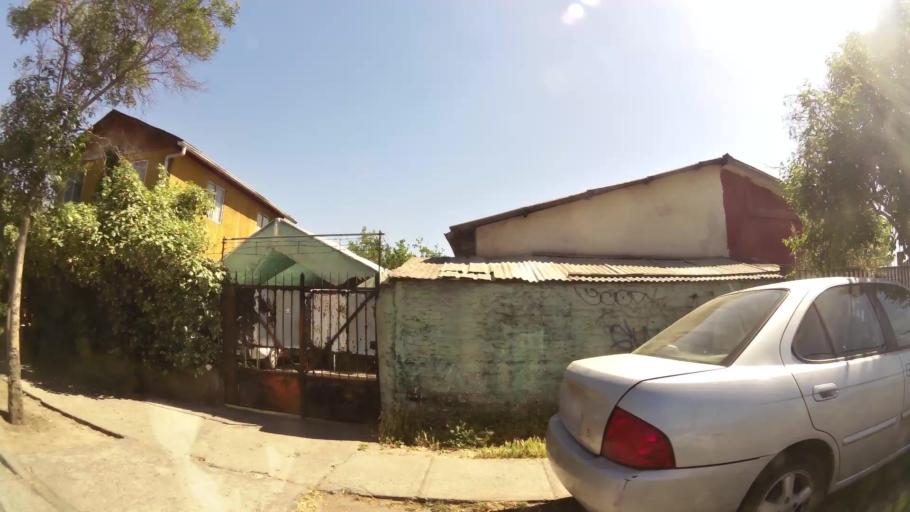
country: CL
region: Santiago Metropolitan
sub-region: Provincia de Santiago
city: La Pintana
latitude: -33.5548
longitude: -70.6612
